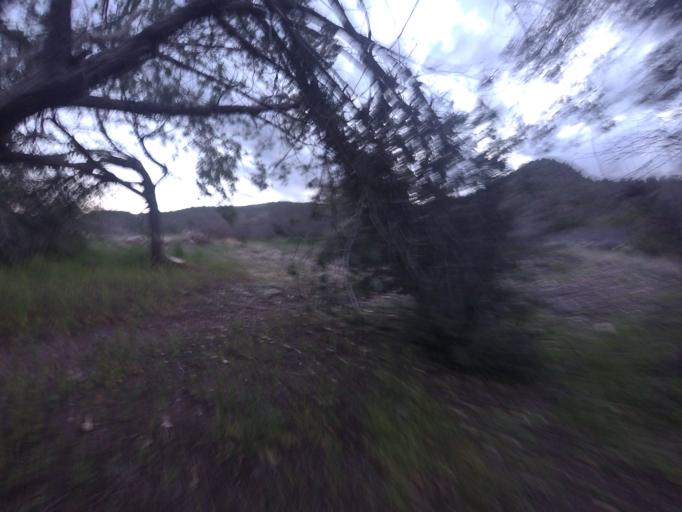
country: US
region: Arizona
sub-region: Gila County
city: Pine
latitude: 34.3846
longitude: -111.6590
